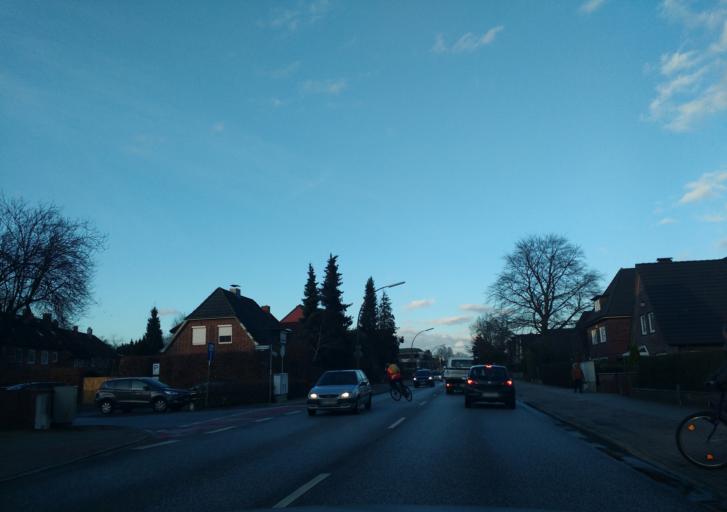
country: DE
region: Schleswig-Holstein
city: Norderstedt
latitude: 53.6791
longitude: 9.9929
